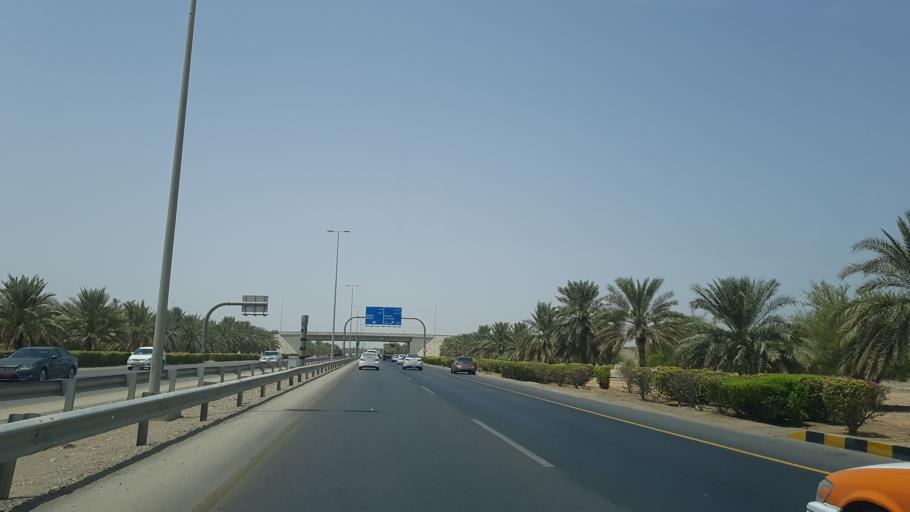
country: OM
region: Muhafazat Masqat
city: As Sib al Jadidah
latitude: 23.5903
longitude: 58.2174
